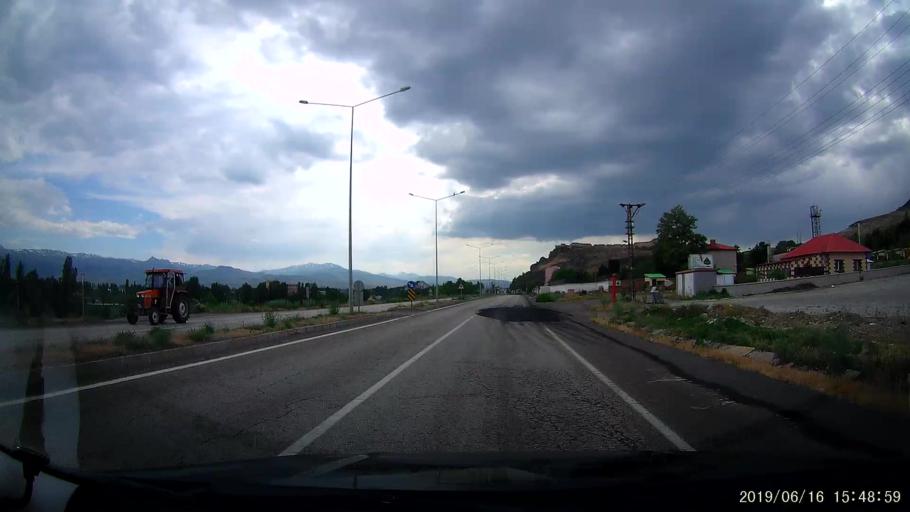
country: TR
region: Erzurum
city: Pasinler
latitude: 39.9795
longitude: 41.6922
